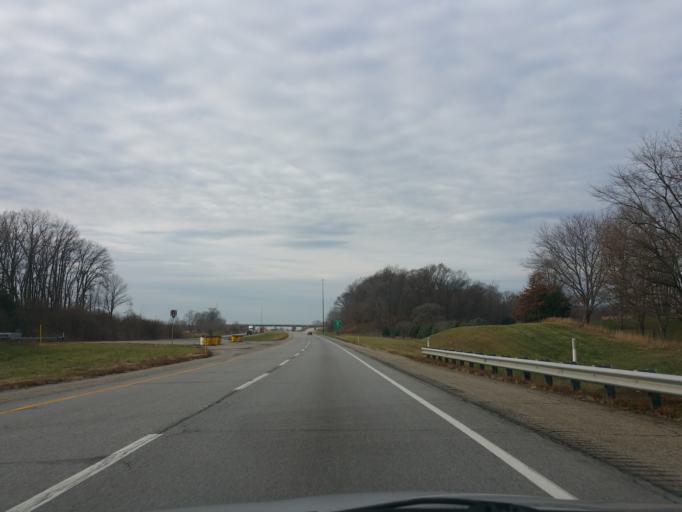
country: US
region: Indiana
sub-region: LaPorte County
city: LaPorte
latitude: 41.6702
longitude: -86.7224
